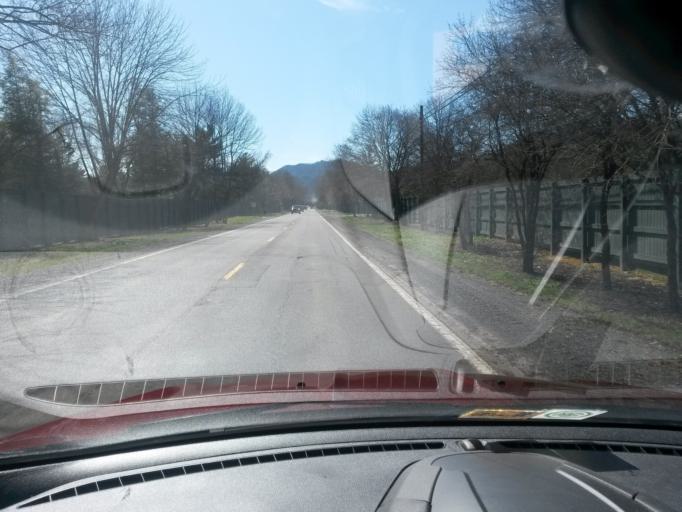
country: US
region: West Virginia
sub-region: Greenbrier County
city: White Sulphur Springs
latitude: 37.7811
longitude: -80.3192
